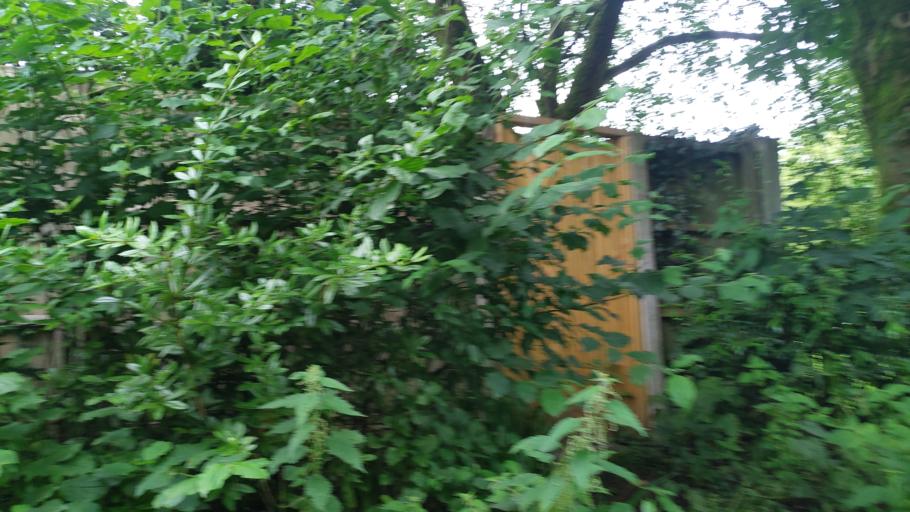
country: GB
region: England
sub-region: Lancashire
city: Euxton
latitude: 53.6589
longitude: -2.6492
